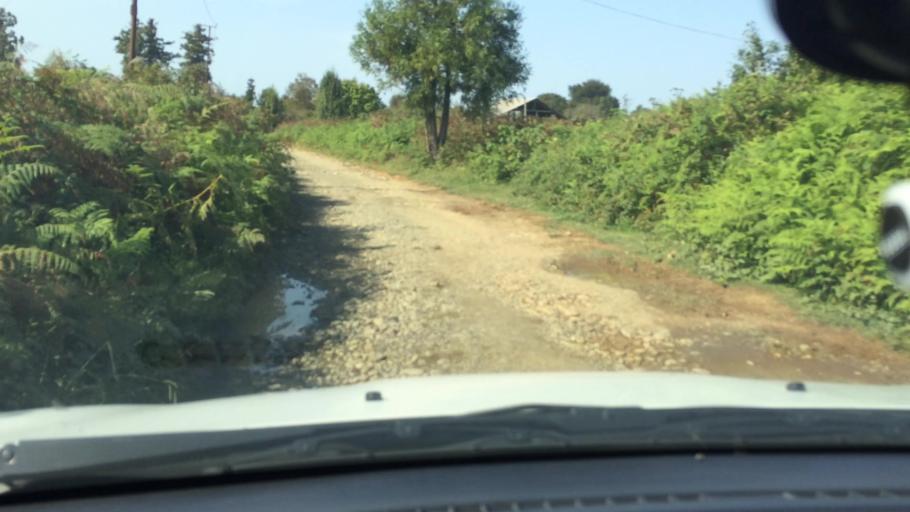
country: GE
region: Ajaria
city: Kobuleti
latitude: 41.8086
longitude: 41.8121
